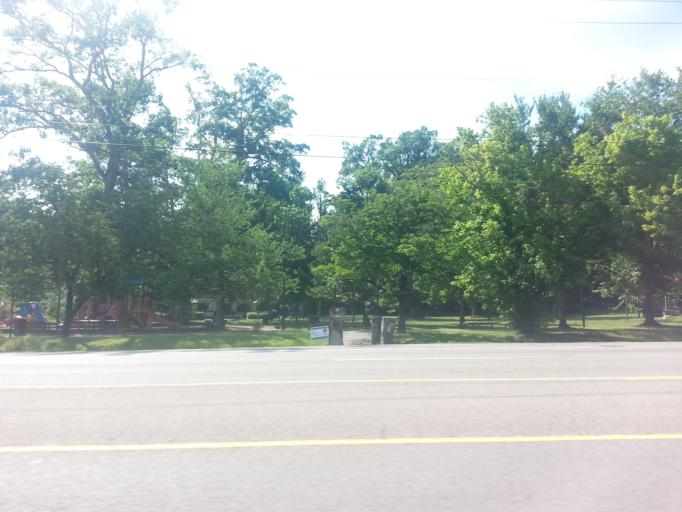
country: US
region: Tennessee
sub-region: Knox County
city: Knoxville
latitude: 36.0366
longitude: -83.9320
